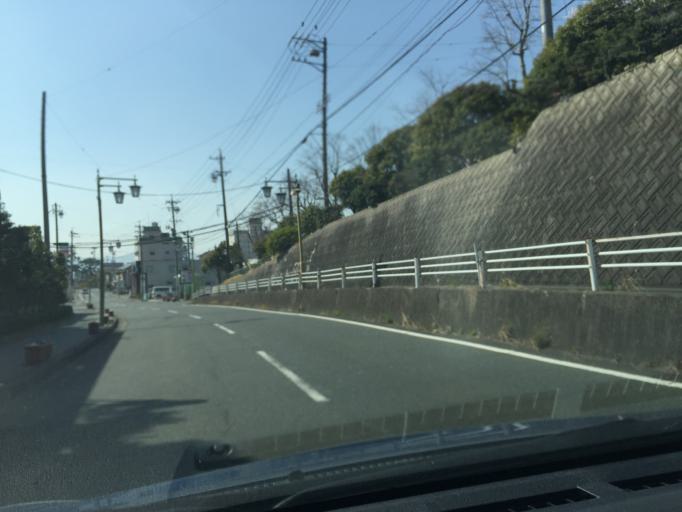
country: JP
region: Shizuoka
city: Kosai-shi
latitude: 34.7639
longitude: 137.6162
